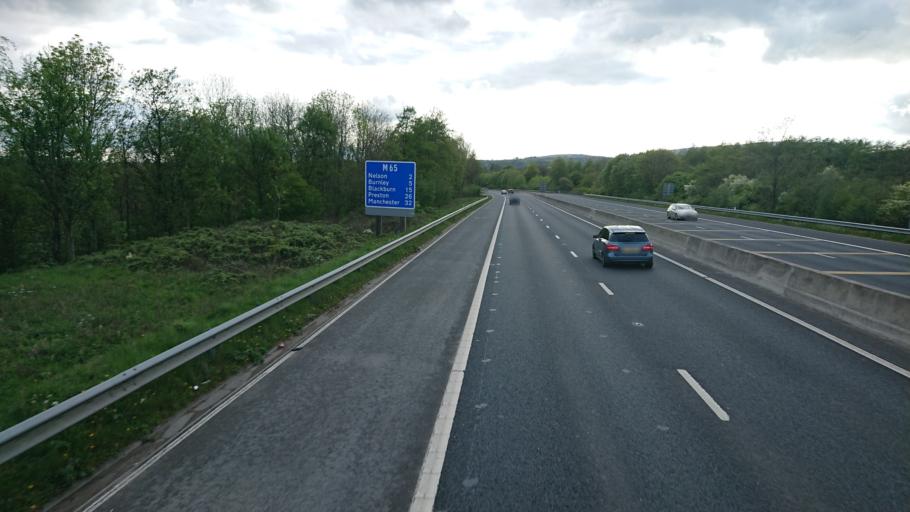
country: GB
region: England
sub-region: Lancashire
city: Nelson
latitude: 53.8538
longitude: -2.1971
